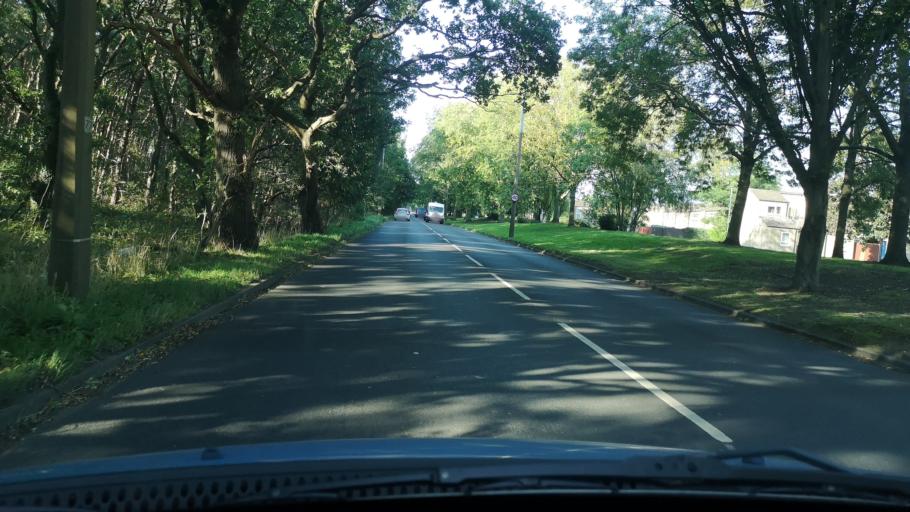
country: GB
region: England
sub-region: North Lincolnshire
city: Scunthorpe
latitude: 53.5765
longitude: -0.6834
